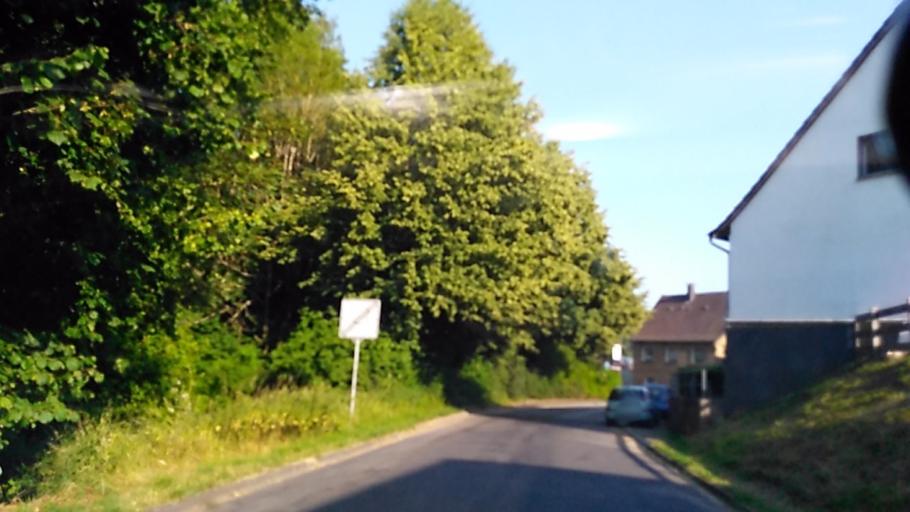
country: DE
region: North Rhine-Westphalia
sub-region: Regierungsbezirk Koln
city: Much
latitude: 50.9058
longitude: 7.4100
